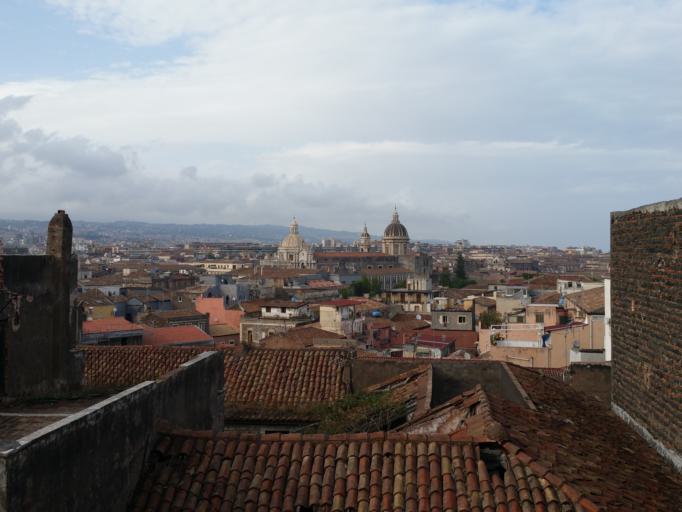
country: IT
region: Sicily
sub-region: Catania
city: Catania
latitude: 37.4990
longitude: 15.0857
